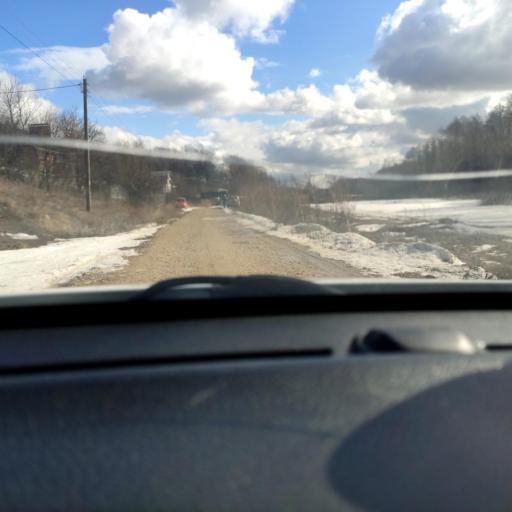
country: RU
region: Voronezj
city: Novaya Usman'
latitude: 51.6887
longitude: 39.3856
